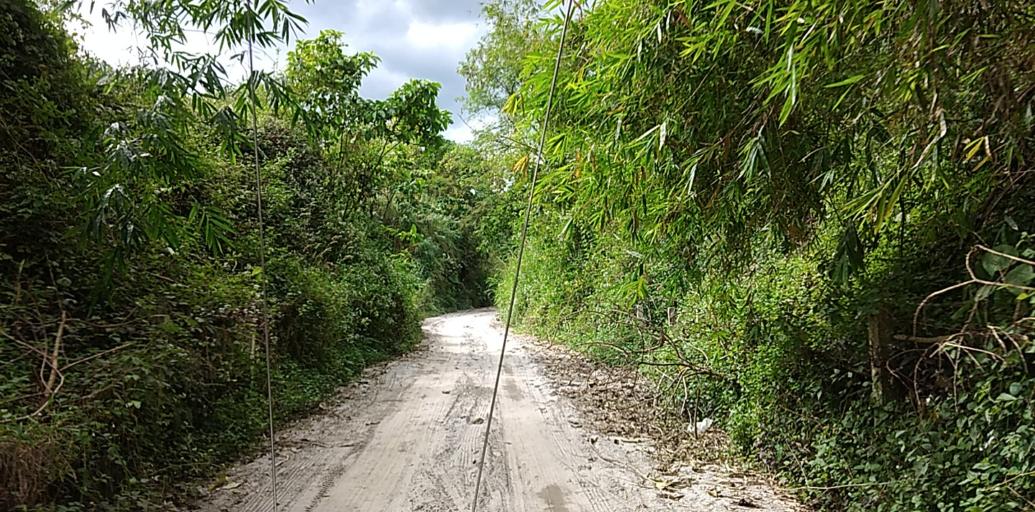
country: PH
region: Central Luzon
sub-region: Province of Pampanga
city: Babo-Pangulo
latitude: 15.1111
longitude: 120.4990
